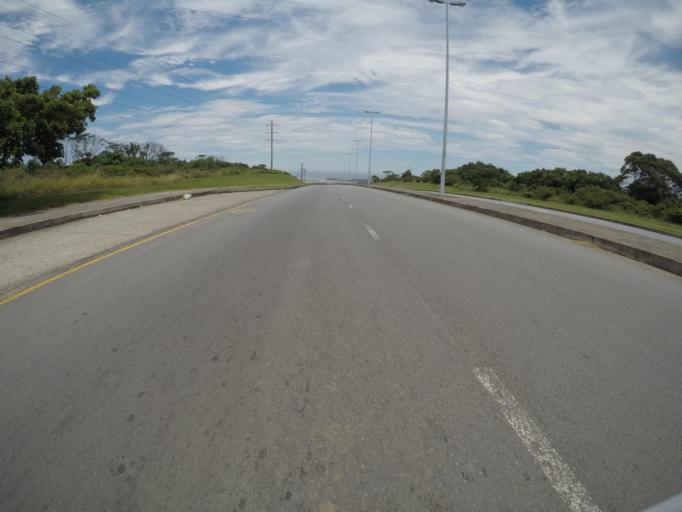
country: ZA
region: Eastern Cape
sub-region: Buffalo City Metropolitan Municipality
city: East London
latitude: -33.0359
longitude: 27.8473
